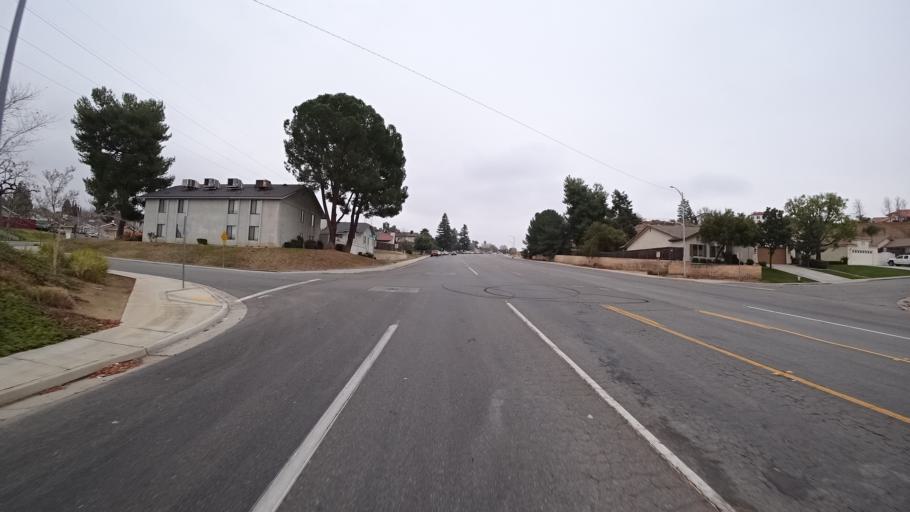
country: US
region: California
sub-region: Kern County
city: Oildale
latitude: 35.4087
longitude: -118.9328
